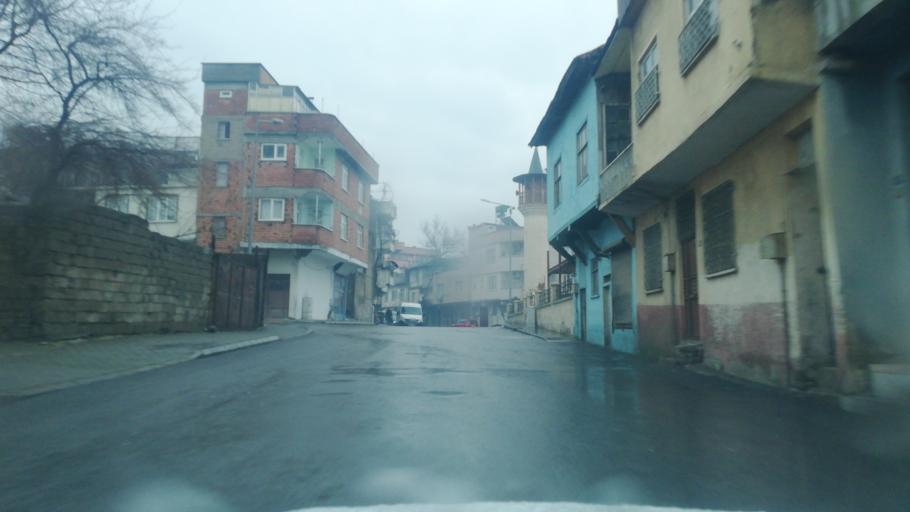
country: TR
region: Kahramanmaras
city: Kahramanmaras
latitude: 37.5814
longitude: 36.9358
